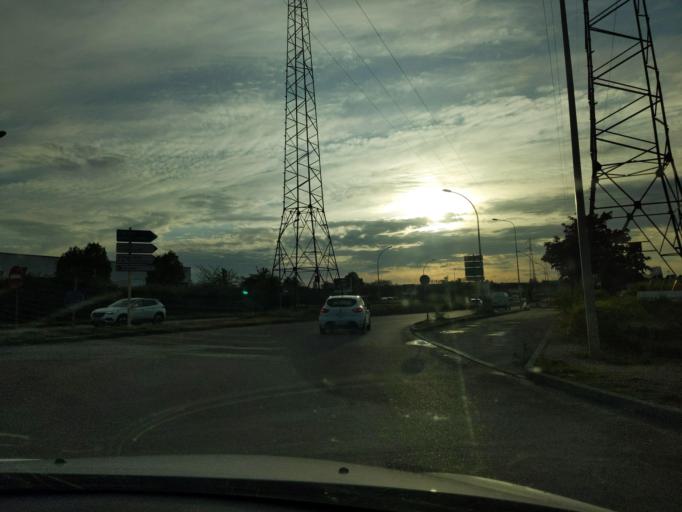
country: FR
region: Bourgogne
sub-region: Departement de la Cote-d'Or
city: Saint-Apollinaire
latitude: 47.3491
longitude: 5.0738
